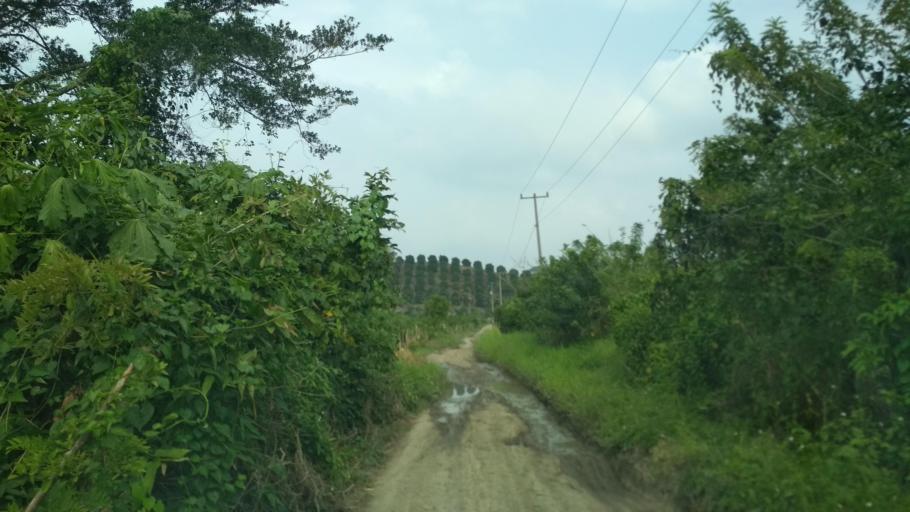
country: MM
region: Kayah
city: Loikaw
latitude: 20.2113
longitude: 97.3152
